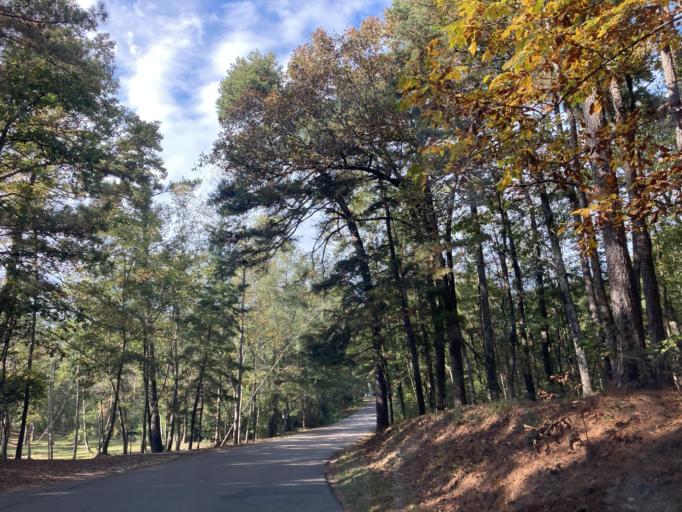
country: US
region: Mississippi
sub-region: Lamar County
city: West Hattiesburg
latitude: 31.3273
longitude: -89.4569
